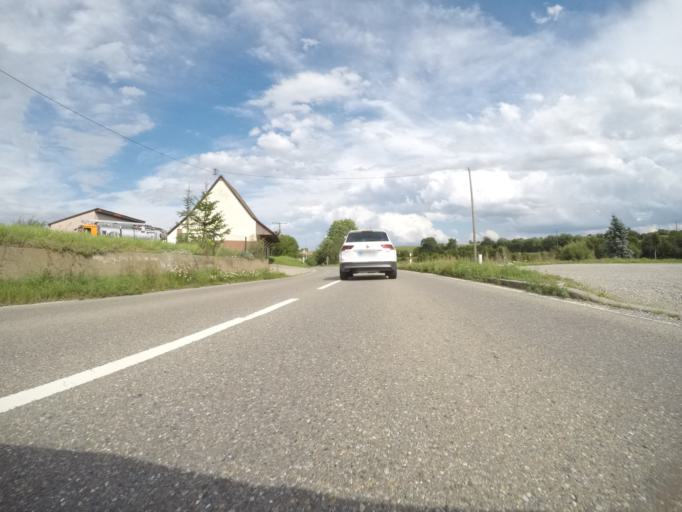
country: DE
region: Baden-Wuerttemberg
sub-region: Karlsruhe Region
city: Schopfloch
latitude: 48.4484
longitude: 8.6200
